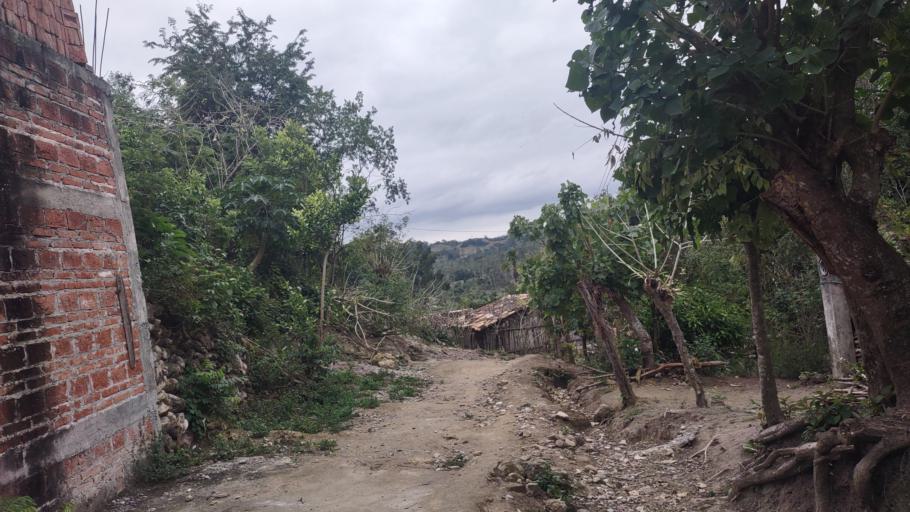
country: MX
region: Veracruz
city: Papantla de Olarte
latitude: 20.4367
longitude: -97.2650
